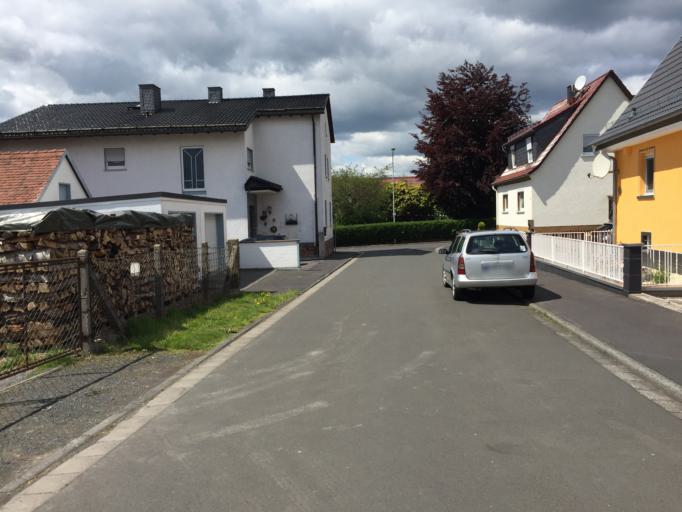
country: DE
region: Hesse
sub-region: Regierungsbezirk Giessen
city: Grunberg
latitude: 50.5748
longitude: 8.9340
